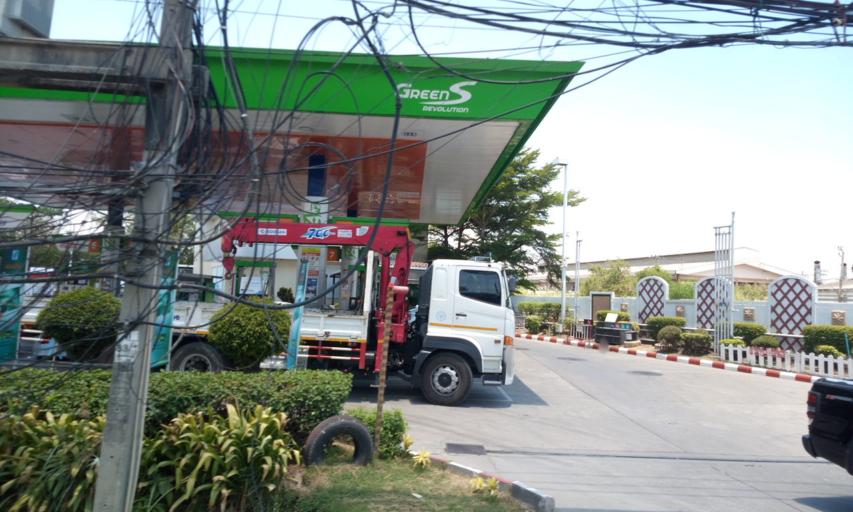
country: TH
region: Bangkok
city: Bang Na
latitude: 13.6198
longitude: 100.7046
